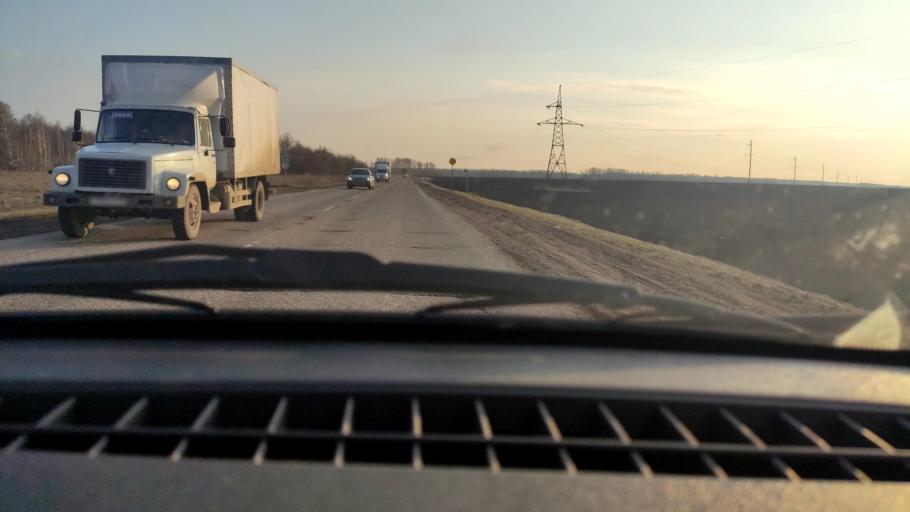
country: RU
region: Bashkortostan
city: Chishmy
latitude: 54.5473
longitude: 55.3271
